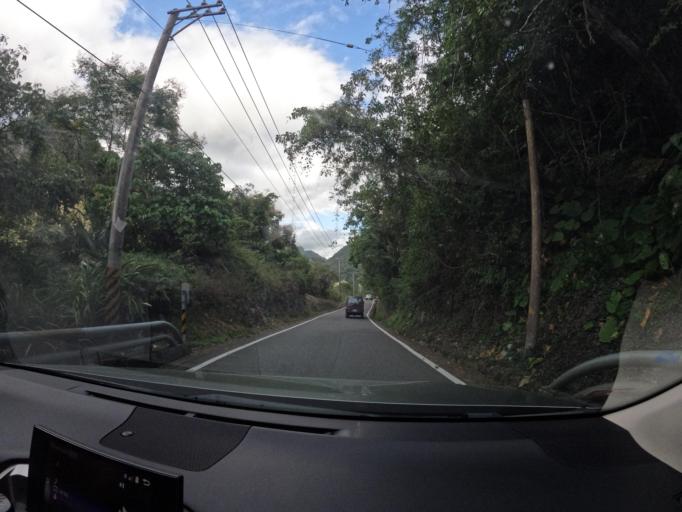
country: TW
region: Taiwan
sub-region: Taitung
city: Taitung
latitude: 23.1409
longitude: 121.0829
